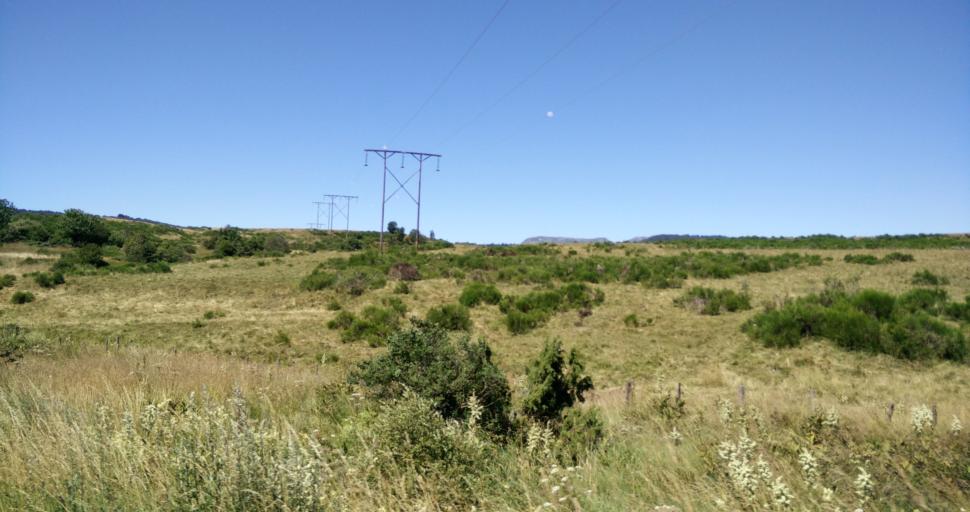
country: FR
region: Auvergne
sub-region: Departement du Puy-de-Dome
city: Mont-Dore
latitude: 45.4665
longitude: 2.9160
